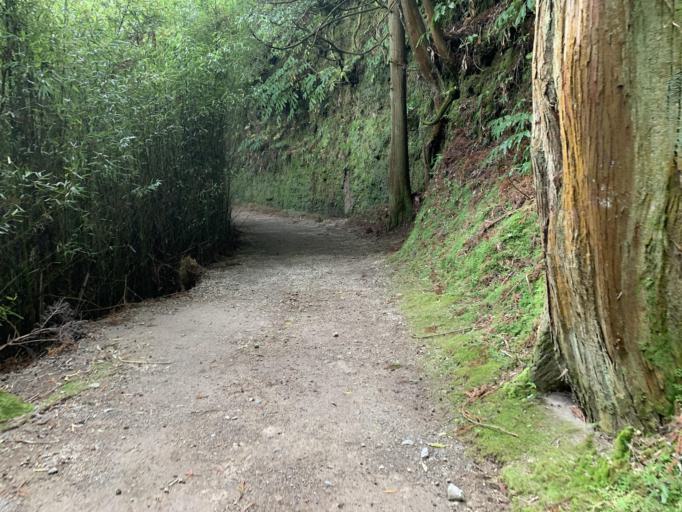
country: PT
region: Azores
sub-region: Povoacao
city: Furnas
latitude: 37.7650
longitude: -25.3335
